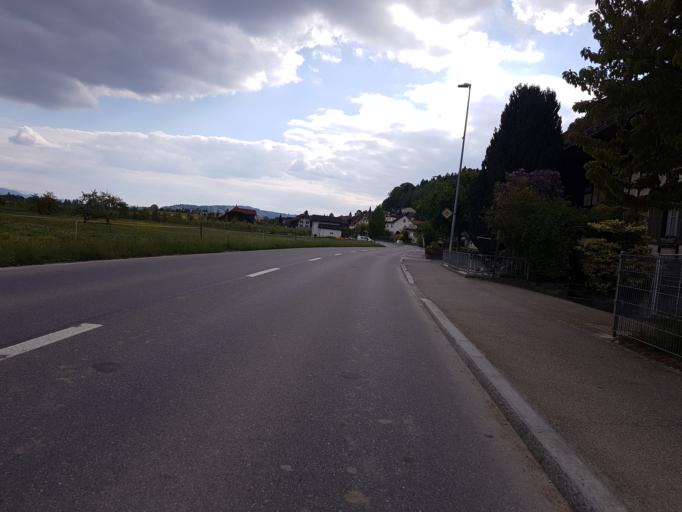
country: CH
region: Bern
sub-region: Biel/Bienne District
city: Orpund
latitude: 47.1485
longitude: 7.3213
